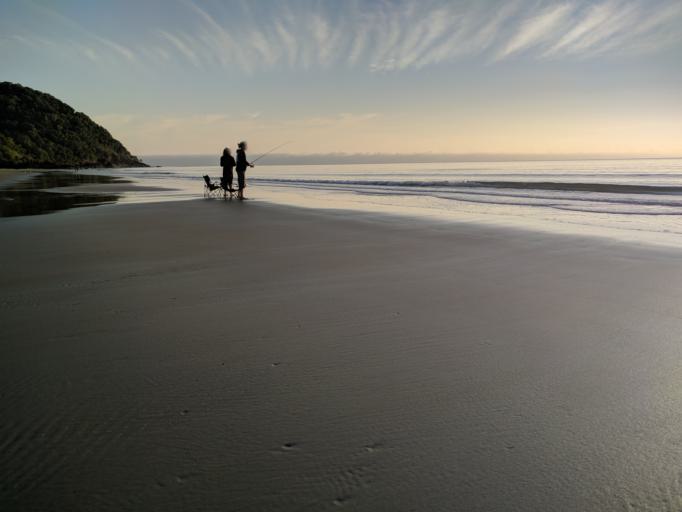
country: AU
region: Queensland
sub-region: Cairns
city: Port Douglas
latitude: -16.1349
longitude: 145.4533
